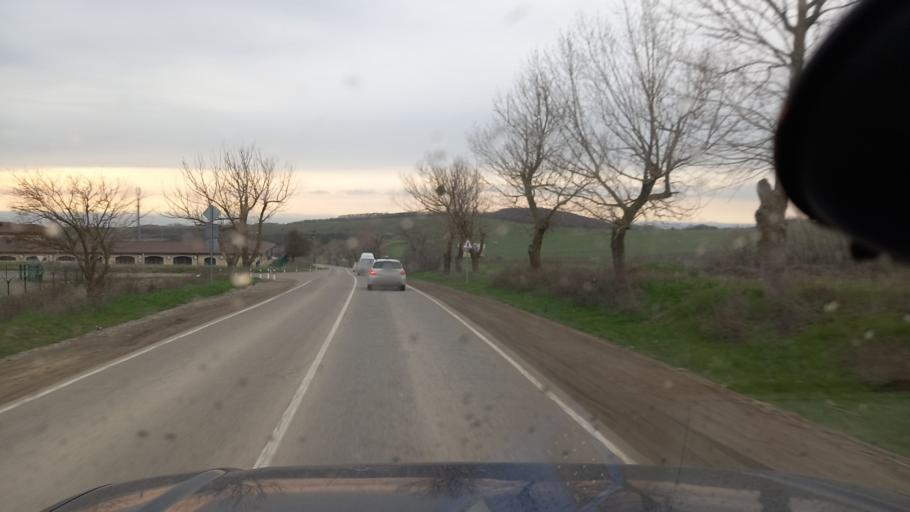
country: RU
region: Krasnodarskiy
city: Sukko
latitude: 44.8400
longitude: 37.3942
